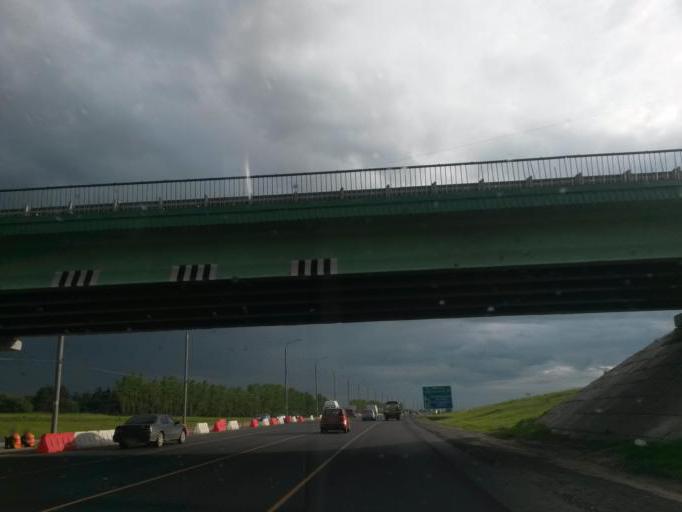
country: RU
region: Moskovskaya
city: Klimovsk
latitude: 55.3441
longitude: 37.5862
